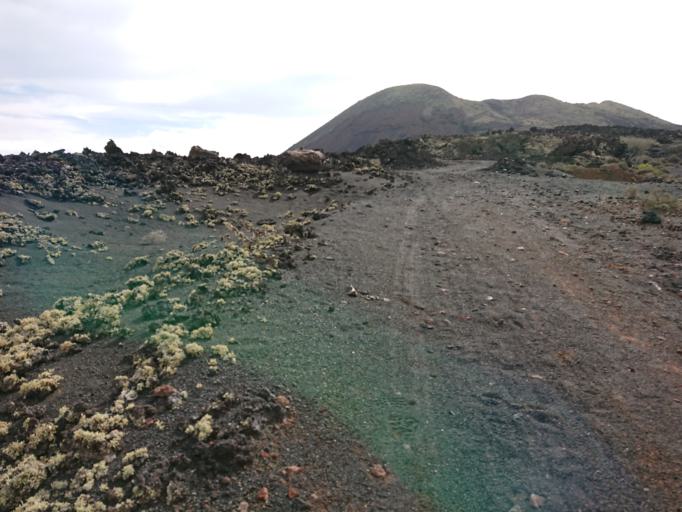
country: ES
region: Canary Islands
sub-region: Provincia de Las Palmas
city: Tinajo
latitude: 29.0130
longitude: -13.6775
